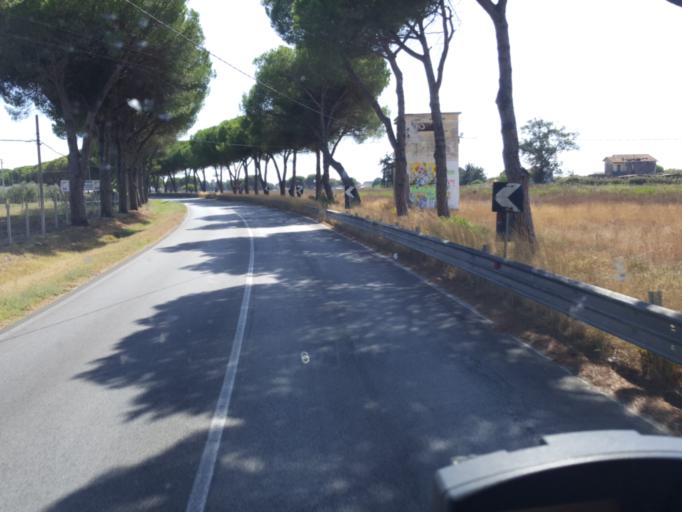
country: IT
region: Latium
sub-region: Provincia di Latina
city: Genio Civile
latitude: 41.5218
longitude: 12.7019
